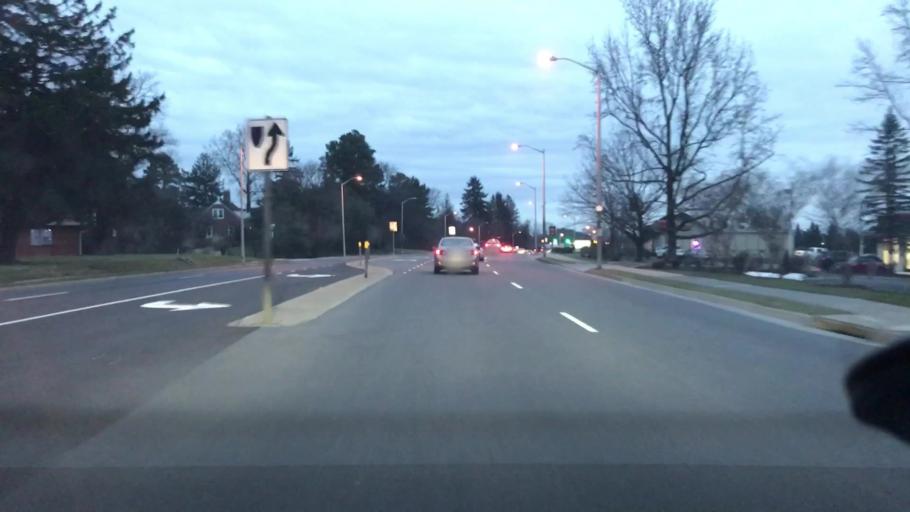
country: US
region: Virginia
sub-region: Montgomery County
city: Blacksburg
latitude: 37.2197
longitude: -80.4033
